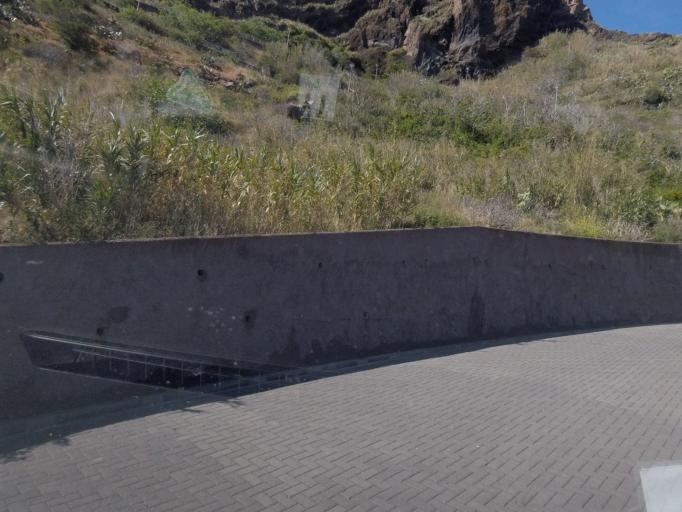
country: PT
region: Madeira
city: Canico
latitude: 32.6396
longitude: -16.8539
